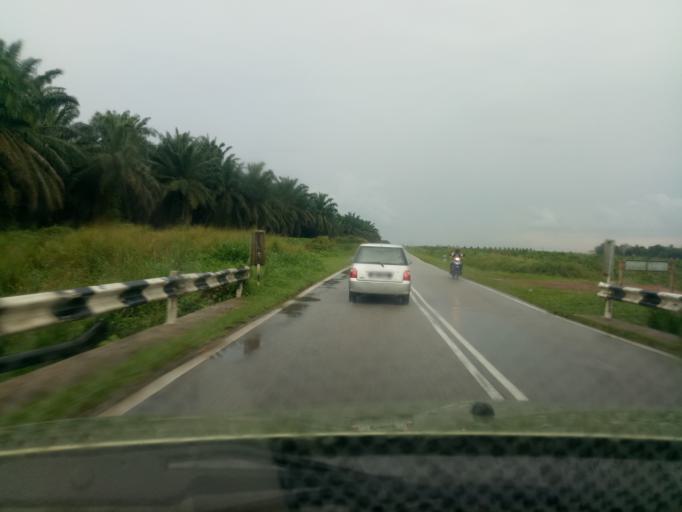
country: MY
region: Kedah
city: Sungai Petani
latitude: 5.5737
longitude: 100.5779
